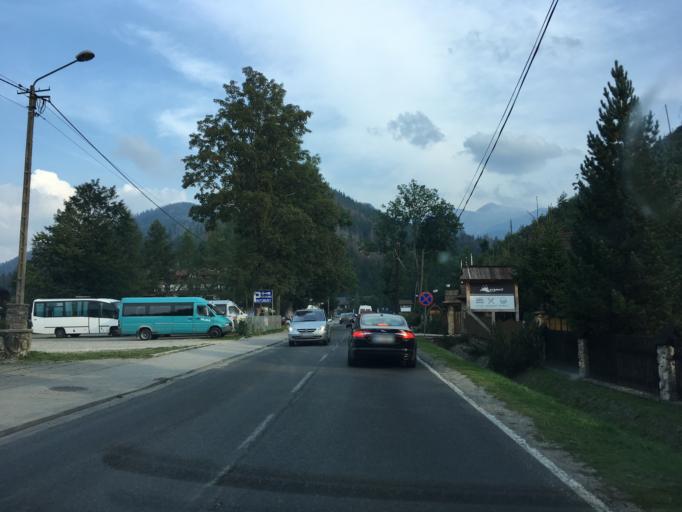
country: PL
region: Lesser Poland Voivodeship
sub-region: Powiat tatrzanski
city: Koscielisko
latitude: 49.2773
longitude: 19.8656
